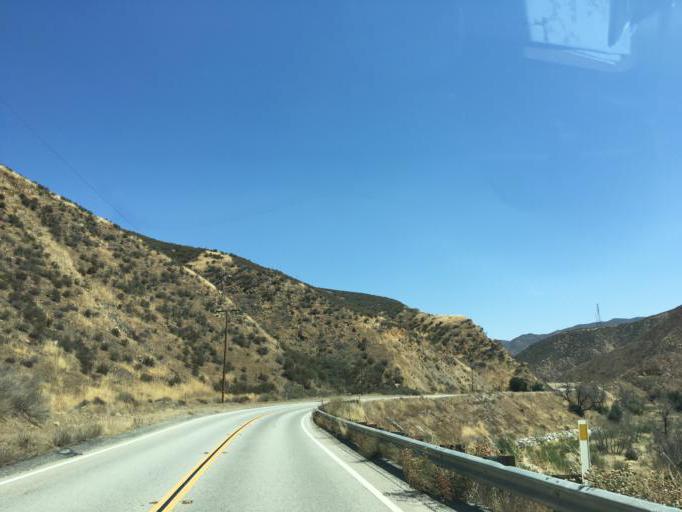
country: US
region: California
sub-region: Los Angeles County
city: Green Valley
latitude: 34.5711
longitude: -118.4641
